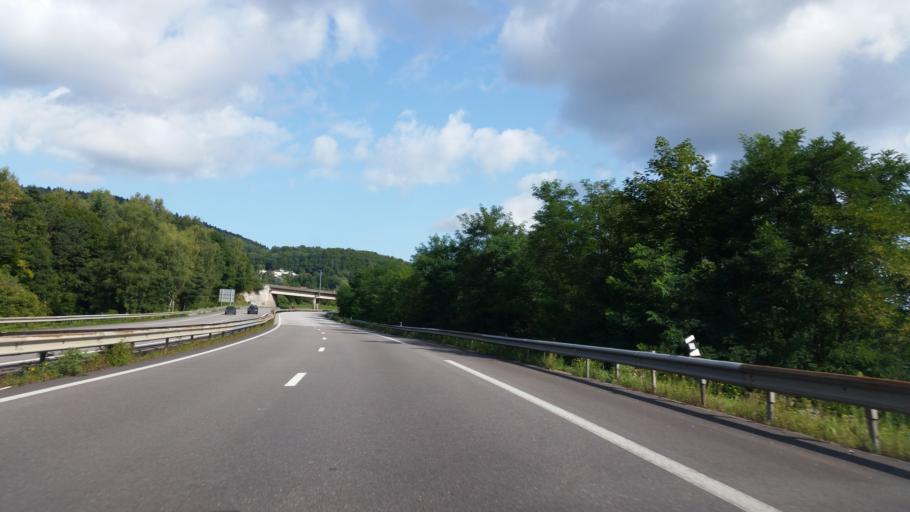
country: FR
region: Lorraine
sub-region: Departement des Vosges
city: Saint-Nabord
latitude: 48.0443
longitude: 6.5840
